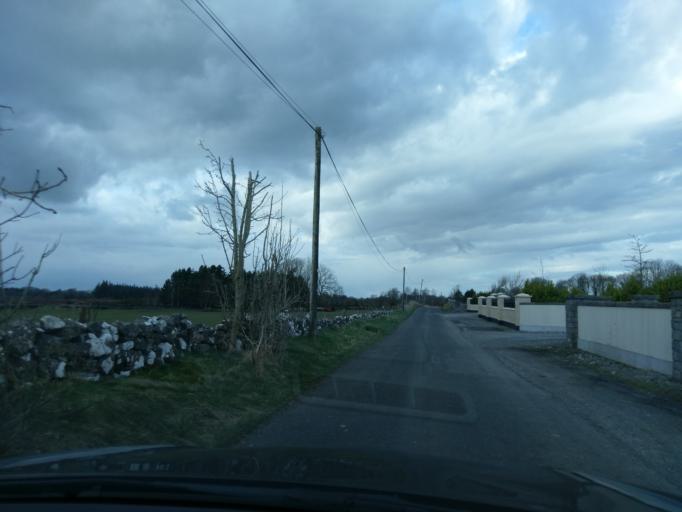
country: IE
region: Connaught
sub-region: County Galway
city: Athenry
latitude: 53.4165
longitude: -8.5858
